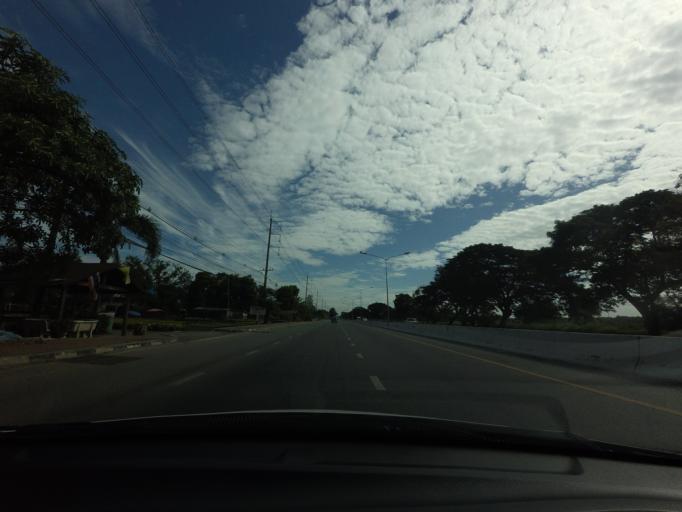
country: TH
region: Pathum Thani
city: Nong Suea
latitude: 14.0814
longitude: 100.9059
